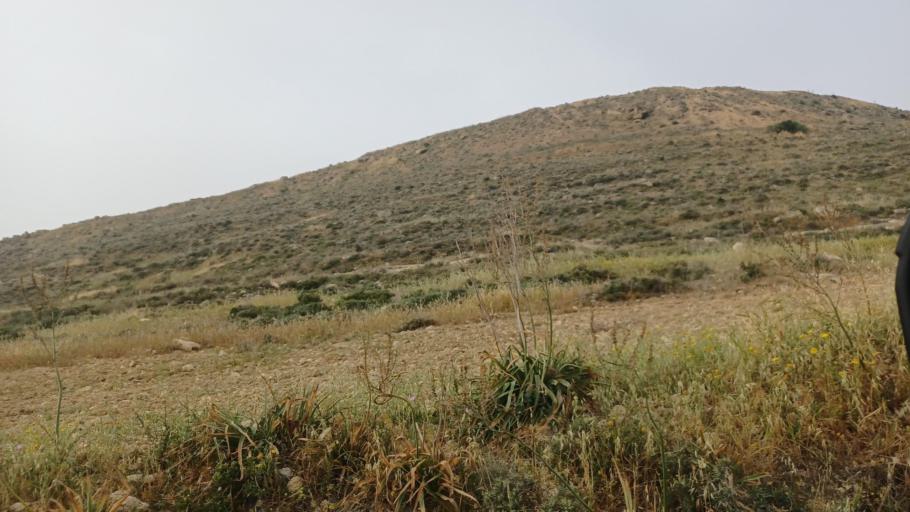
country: CY
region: Lefkosia
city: Mammari
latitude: 35.1813
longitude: 33.1852
